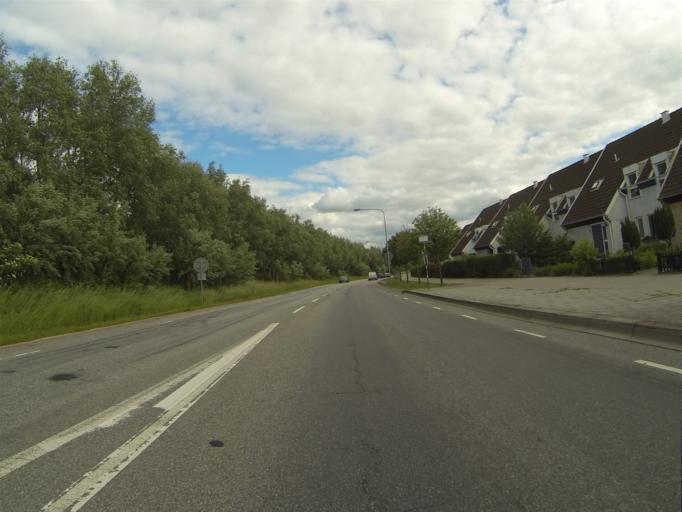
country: SE
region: Skane
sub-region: Burlovs Kommun
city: Arloev
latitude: 55.6165
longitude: 13.0616
